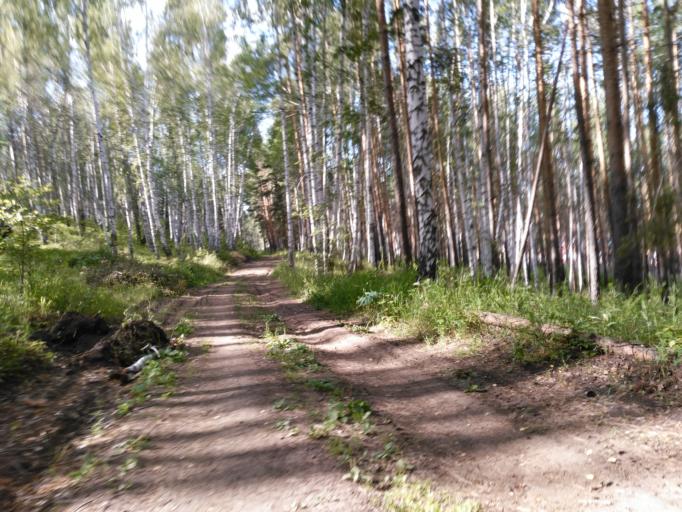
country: RU
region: Bashkortostan
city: Uchaly
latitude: 54.3263
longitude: 59.3612
